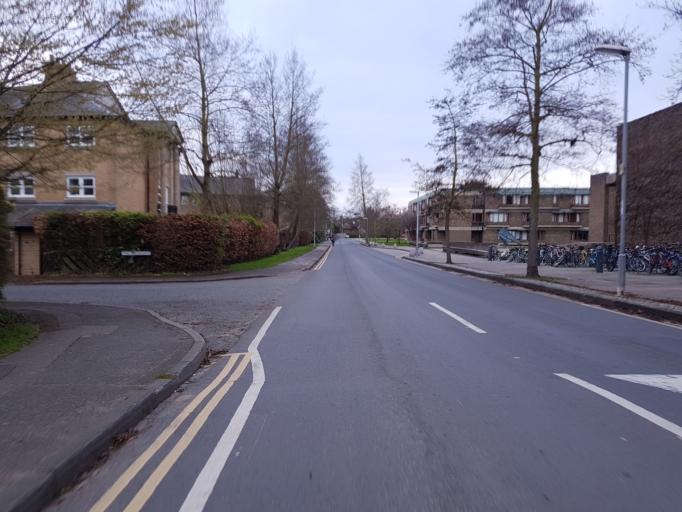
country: GB
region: England
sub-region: Cambridgeshire
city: Cambridge
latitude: 52.2130
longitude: 0.1045
